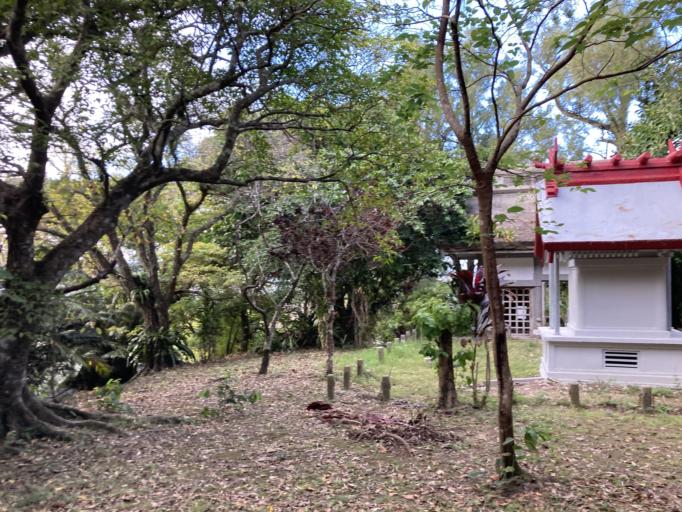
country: JP
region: Okinawa
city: Ginowan
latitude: 26.1656
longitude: 127.7875
